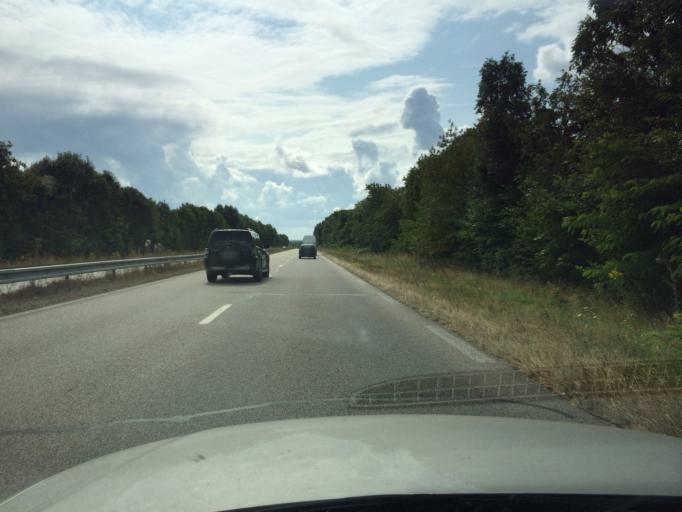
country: FR
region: Lower Normandy
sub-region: Departement de la Manche
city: Montebourg
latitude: 49.4890
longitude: -1.4018
